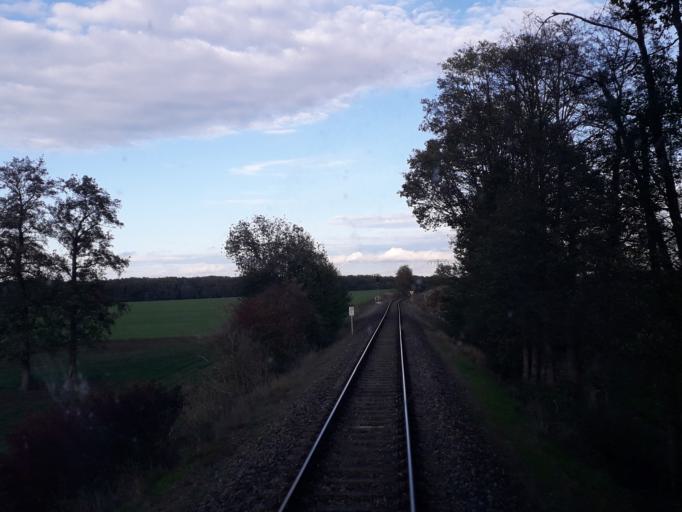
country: DE
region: Brandenburg
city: Gross Pankow
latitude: 53.0998
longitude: 11.9902
